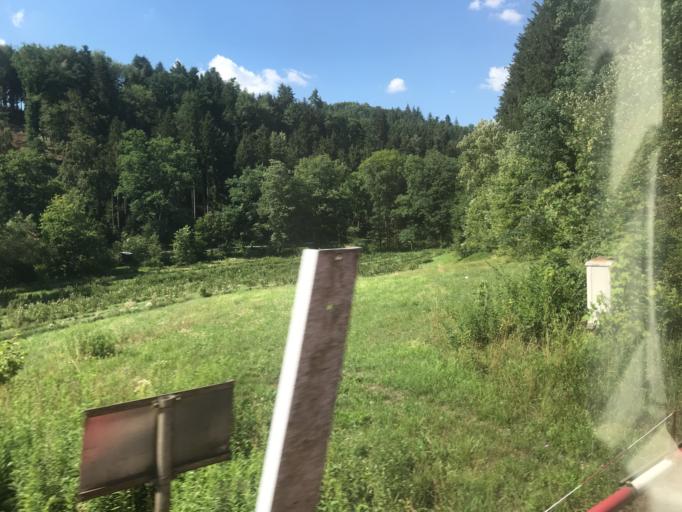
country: AT
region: Upper Austria
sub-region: Politischer Bezirk Urfahr-Umgebung
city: Engerwitzdorf
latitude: 48.2817
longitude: 14.4605
